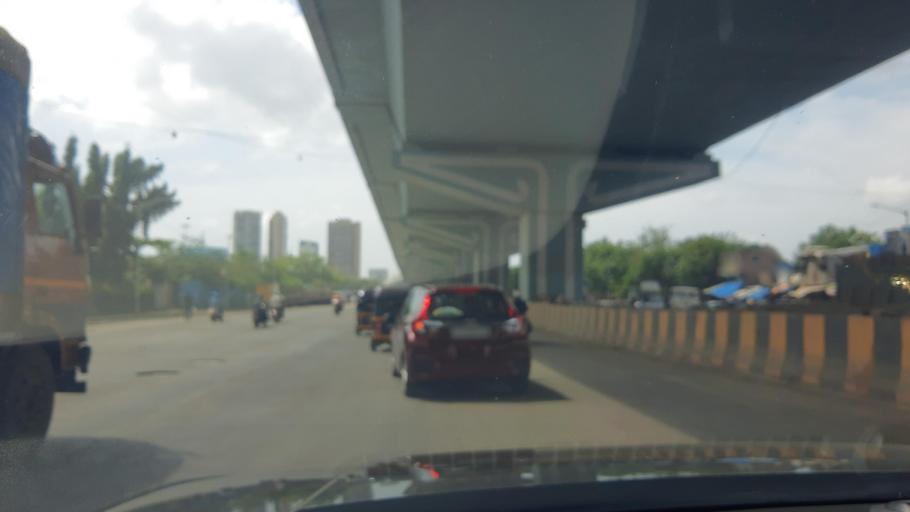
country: IN
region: Maharashtra
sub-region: Mumbai Suburban
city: Mumbai
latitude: 19.0593
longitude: 72.9234
